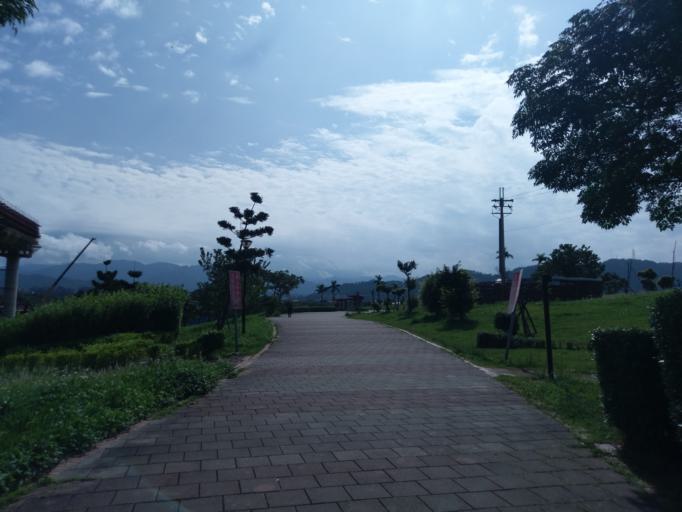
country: TW
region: Taiwan
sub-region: Taoyuan
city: Taoyuan
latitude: 24.9535
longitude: 121.3593
